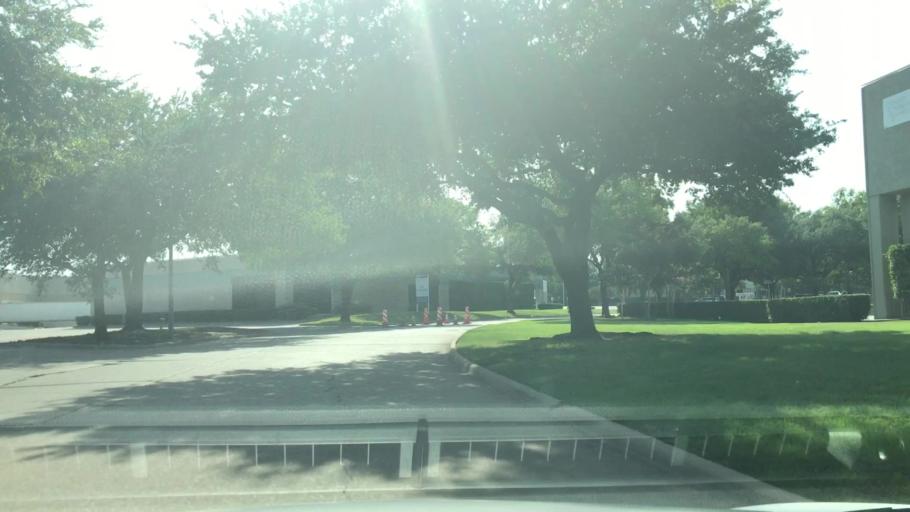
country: US
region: Texas
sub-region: Dallas County
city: Richardson
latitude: 32.8905
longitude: -96.7018
